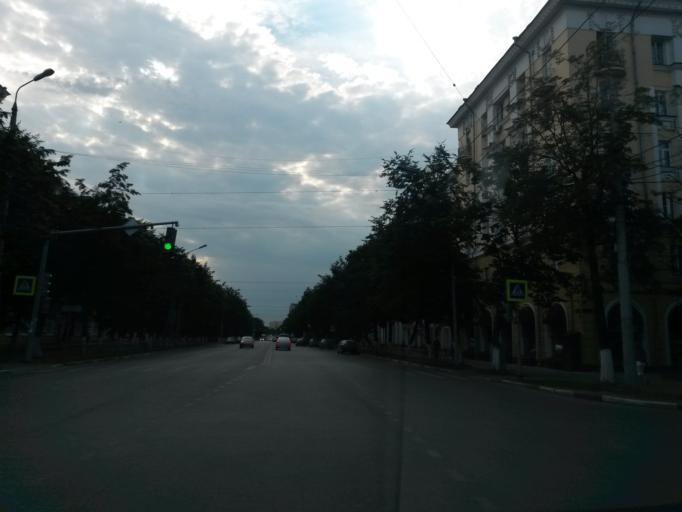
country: RU
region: Jaroslavl
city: Yaroslavl
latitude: 57.6264
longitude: 39.8625
